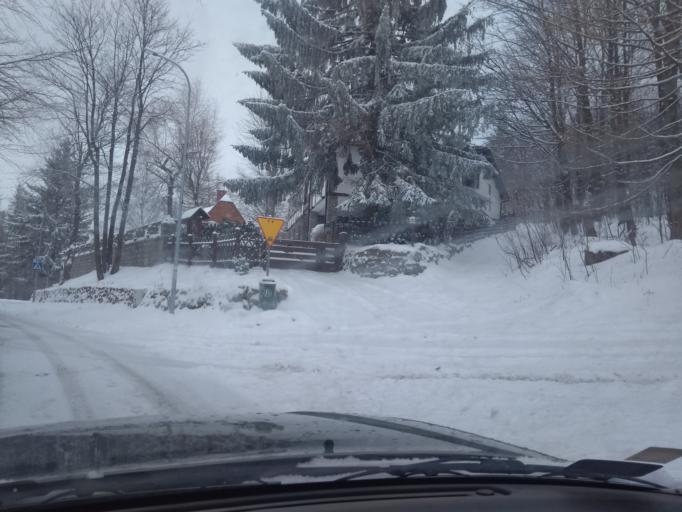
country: PL
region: Lower Silesian Voivodeship
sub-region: Powiat jeleniogorski
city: Karpacz
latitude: 50.7839
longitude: 15.7225
